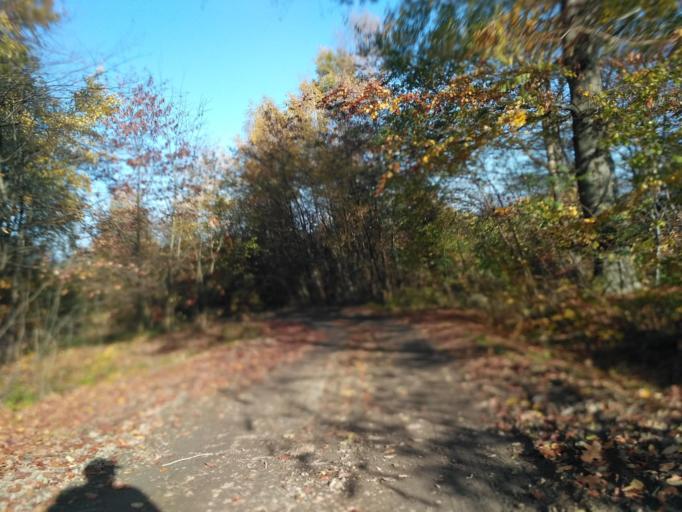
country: PL
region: Subcarpathian Voivodeship
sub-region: Powiat rzeszowski
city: Blazowa
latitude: 49.8584
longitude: 22.0817
